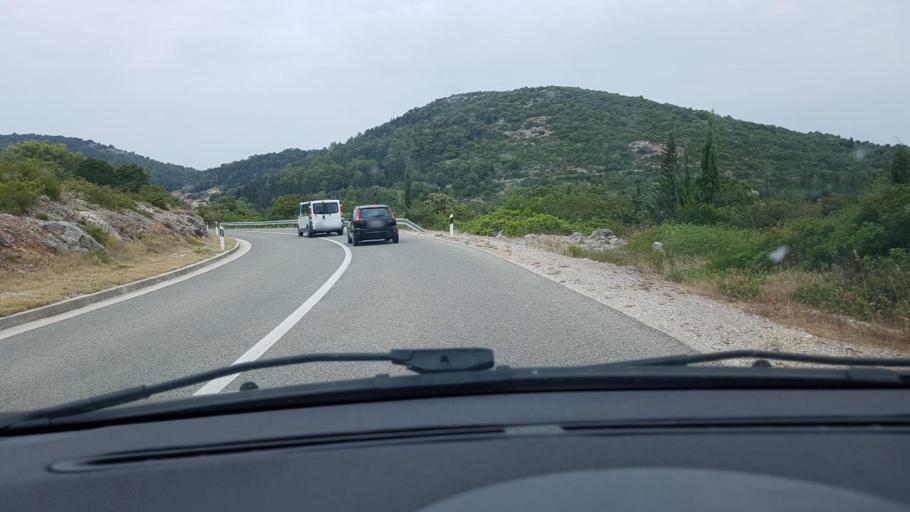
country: HR
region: Dubrovacko-Neretvanska
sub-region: Grad Korcula
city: Zrnovo
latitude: 42.9457
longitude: 17.0461
